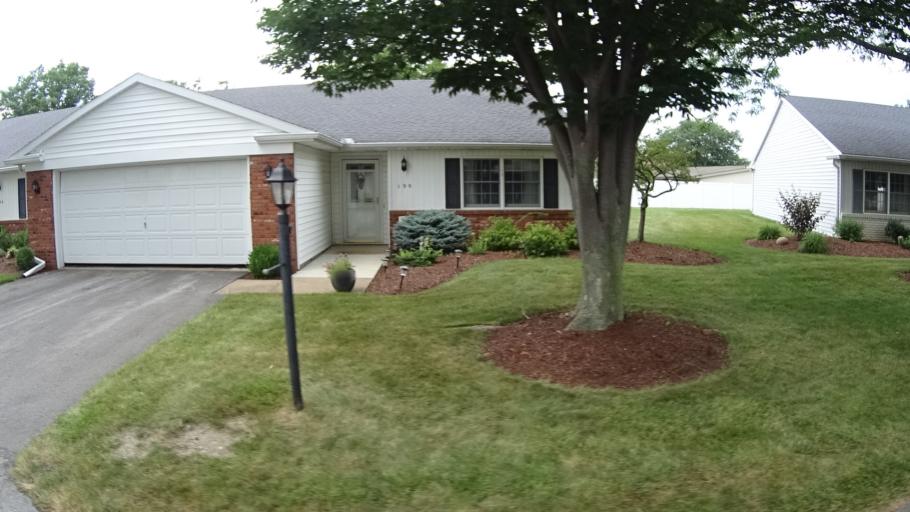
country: US
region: Ohio
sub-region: Erie County
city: Sandusky
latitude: 41.4391
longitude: -82.7672
